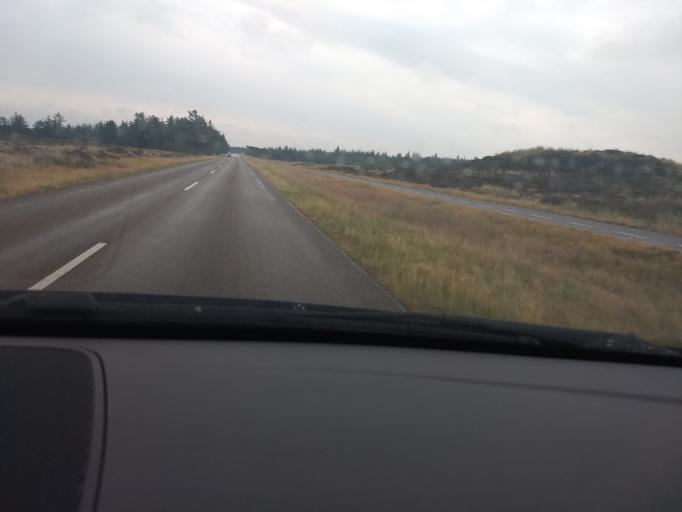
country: DK
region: South Denmark
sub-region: Fano Kommune
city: Nordby
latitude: 55.4106
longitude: 8.4111
